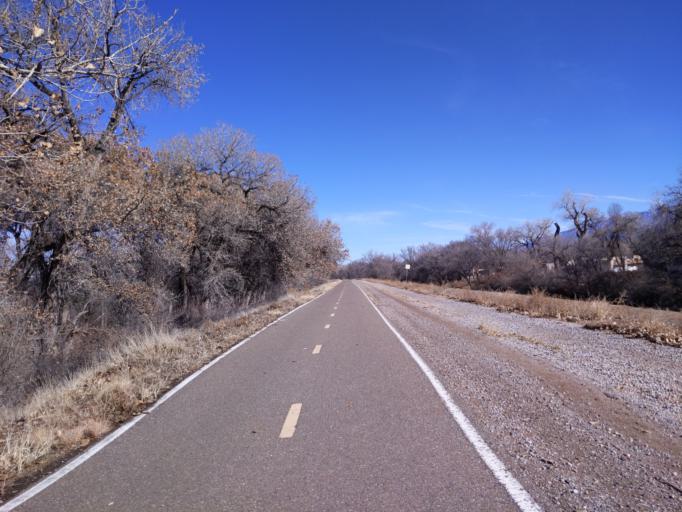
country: US
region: New Mexico
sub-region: Bernalillo County
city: Lee Acres
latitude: 35.1468
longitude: -106.6735
